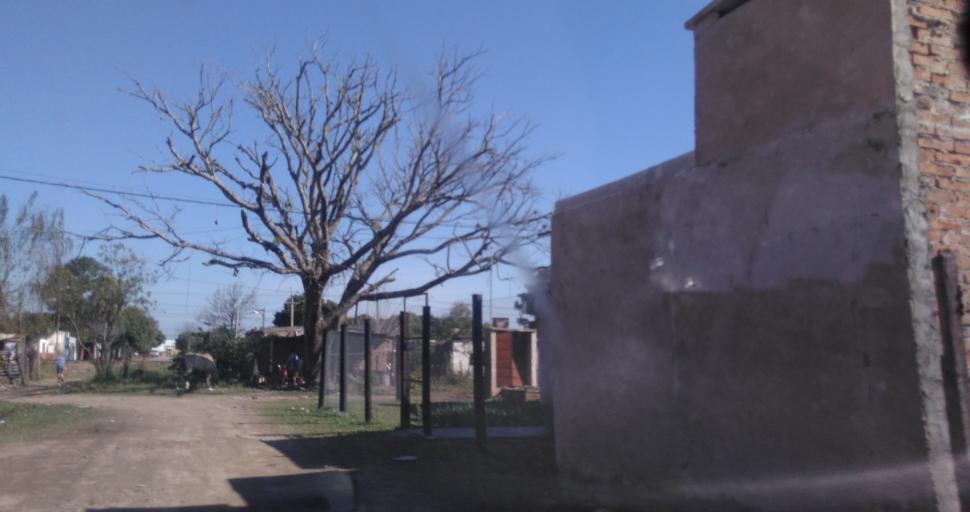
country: AR
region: Chaco
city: Fontana
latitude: -27.4325
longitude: -59.0156
